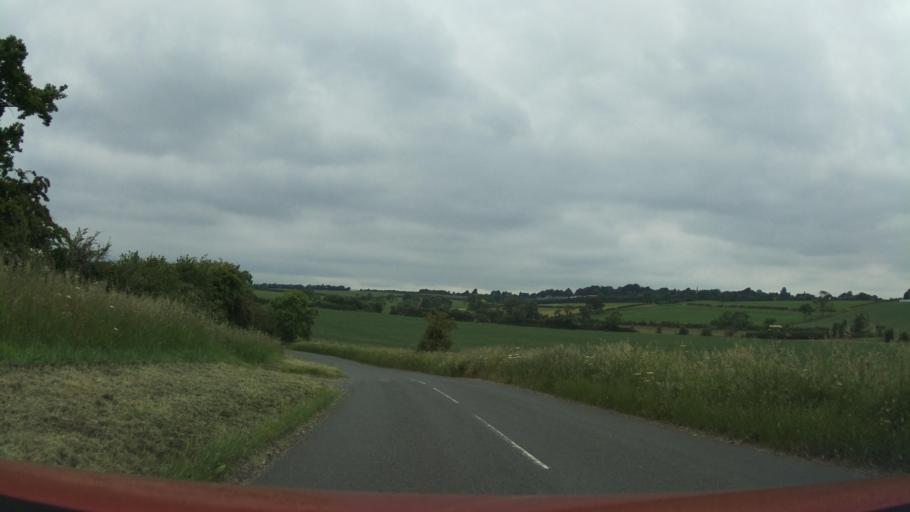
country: GB
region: England
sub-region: District of Rutland
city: Langham
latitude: 52.6744
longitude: -0.7861
